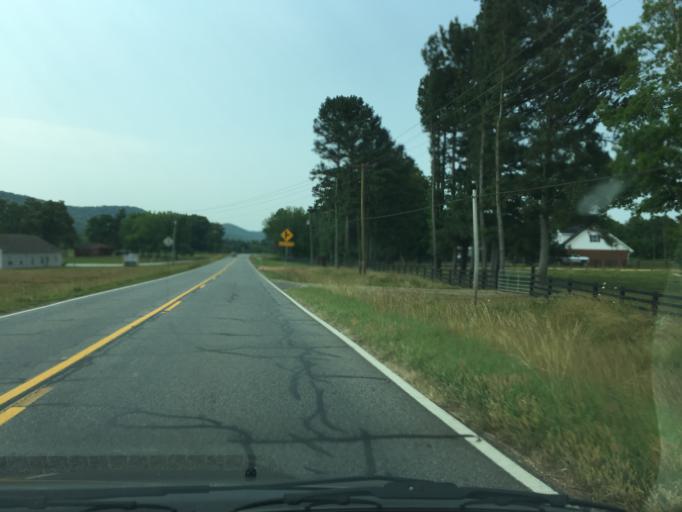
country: US
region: Georgia
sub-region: Catoosa County
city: Ringgold
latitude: 34.8567
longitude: -85.1437
